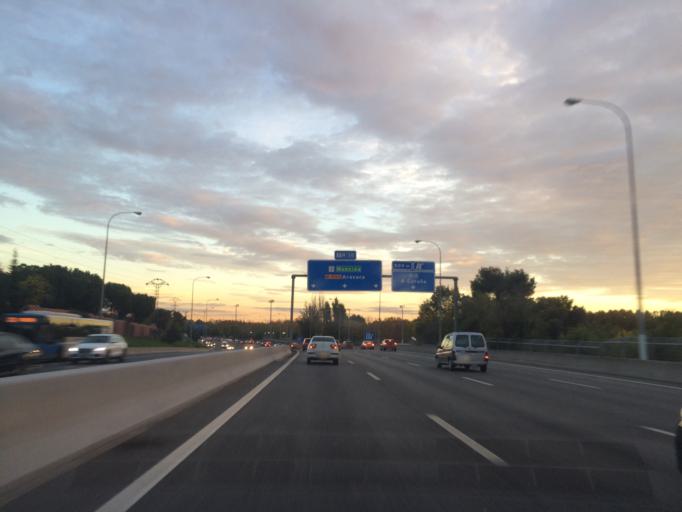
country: ES
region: Madrid
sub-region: Provincia de Madrid
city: Tetuan de las Victorias
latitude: 40.4664
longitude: -3.7494
